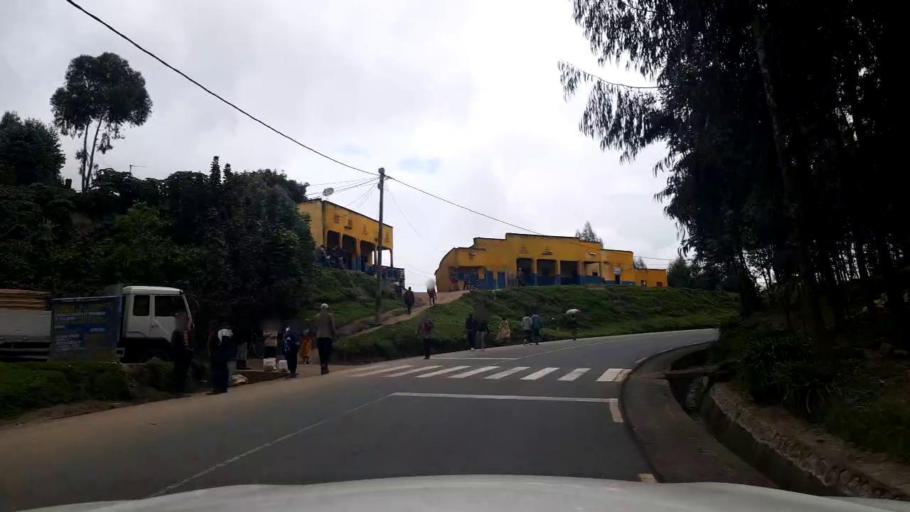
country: RW
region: Northern Province
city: Musanze
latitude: -1.6512
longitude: 29.5097
